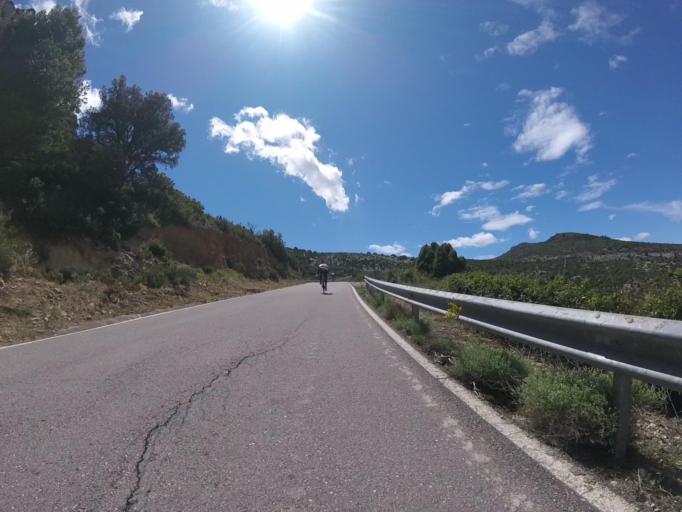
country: ES
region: Valencia
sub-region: Provincia de Castello
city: Sierra-Engarceran
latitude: 40.2835
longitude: -0.0329
